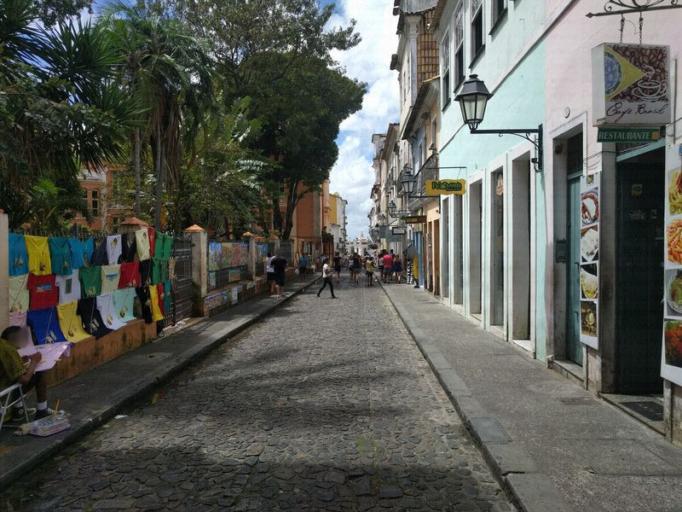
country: BR
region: Bahia
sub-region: Salvador
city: Salvador
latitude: -12.9728
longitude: -38.5096
